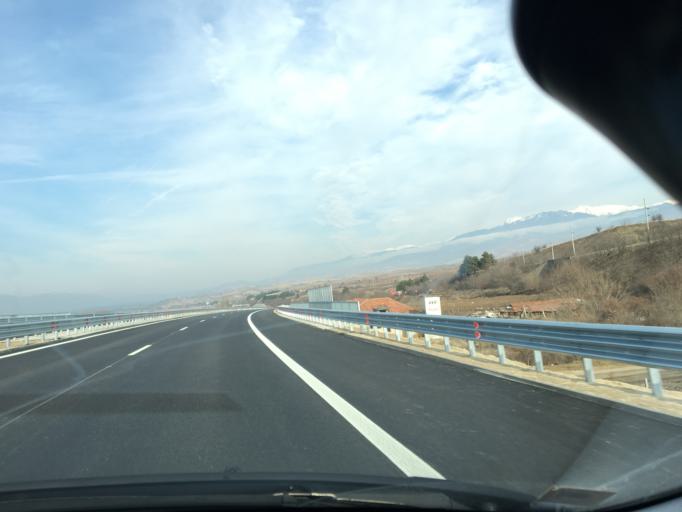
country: BG
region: Blagoevgrad
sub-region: Obshtina Sandanski
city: Sandanski
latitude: 41.5625
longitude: 23.2409
